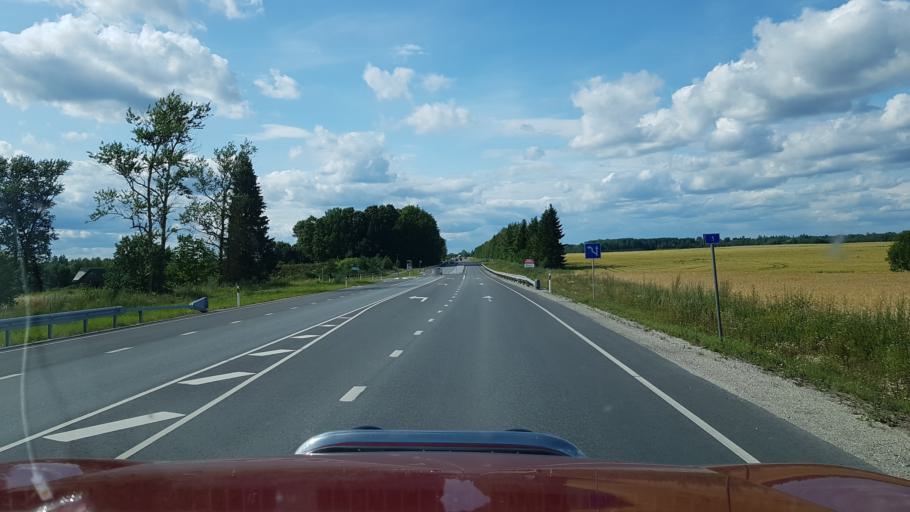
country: EE
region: Tartu
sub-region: Tartu linn
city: Tartu
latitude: 58.4181
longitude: 26.7025
